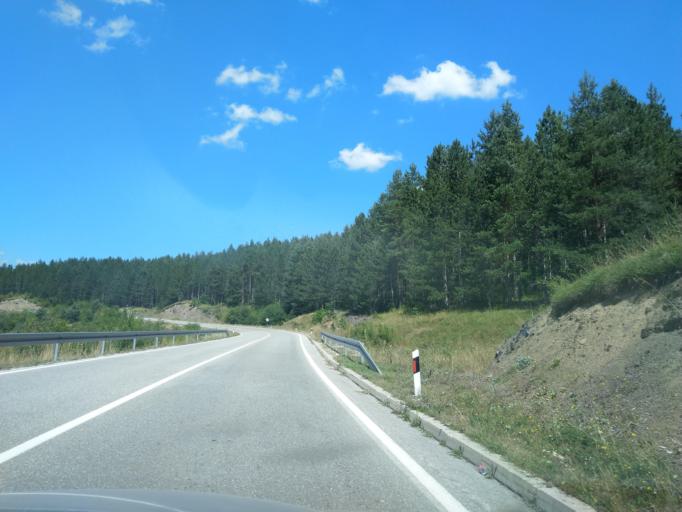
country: RS
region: Central Serbia
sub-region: Zlatiborski Okrug
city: Sjenica
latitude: 43.3030
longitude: 19.9299
